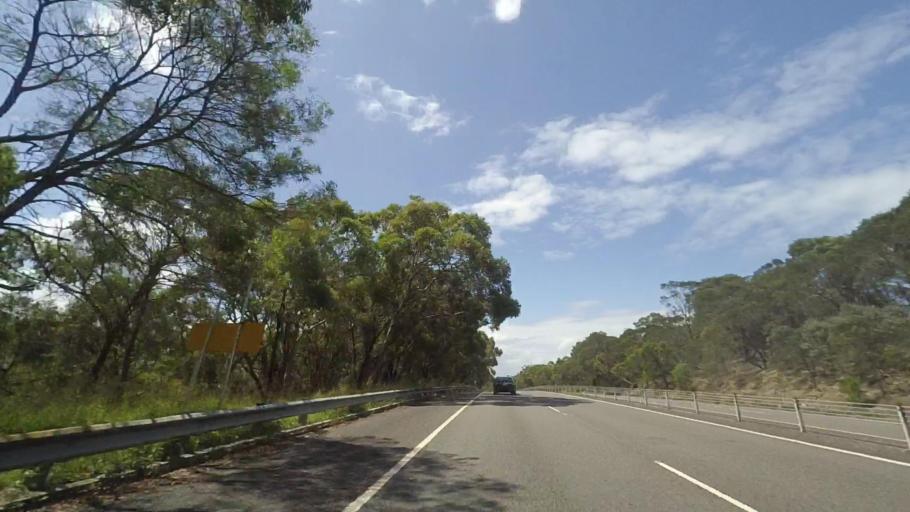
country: AU
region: New South Wales
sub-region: Wyong Shire
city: Kingfisher Shores
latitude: -33.1503
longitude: 151.6134
